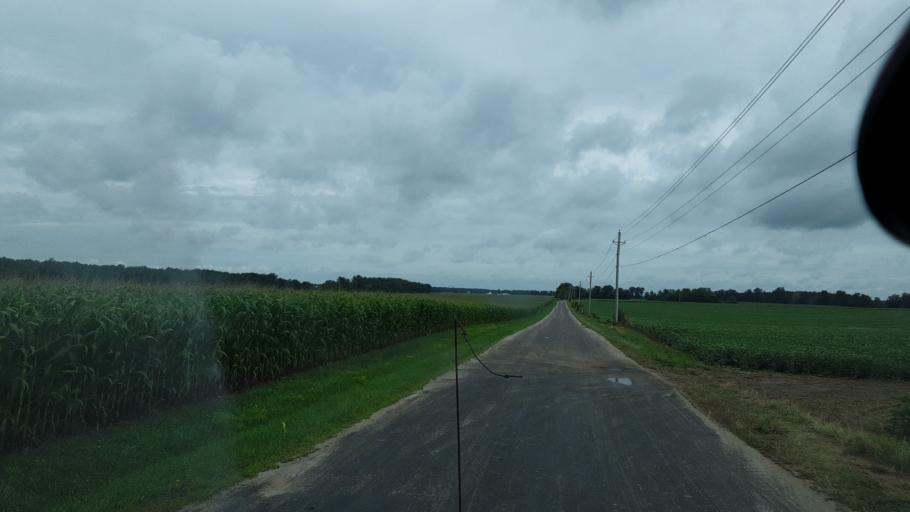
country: US
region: Indiana
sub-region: Adams County
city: Geneva
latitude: 40.5280
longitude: -85.0101
